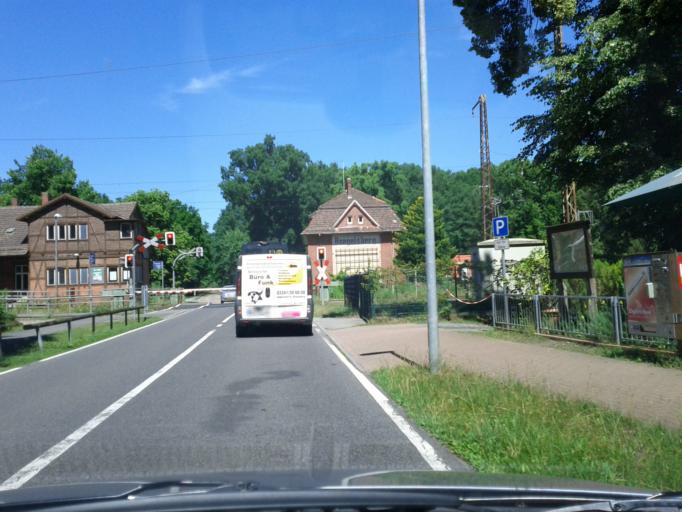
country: DE
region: Brandenburg
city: Spreenhagen
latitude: 52.3998
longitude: 13.9214
